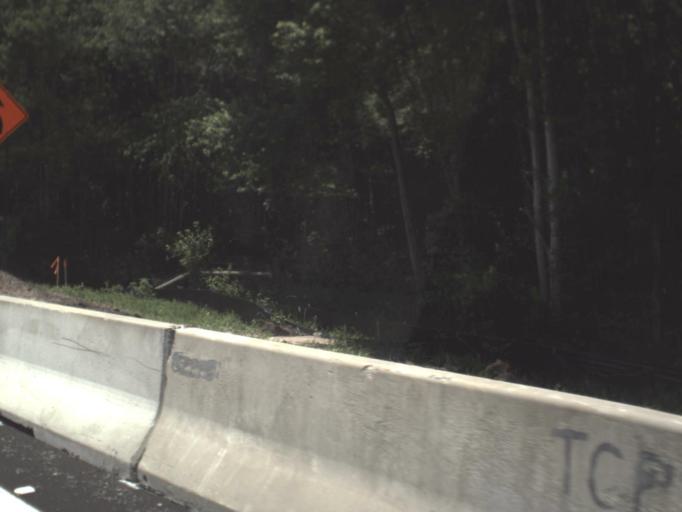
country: US
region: Florida
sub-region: Columbia County
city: Watertown
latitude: 30.2451
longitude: -82.5637
